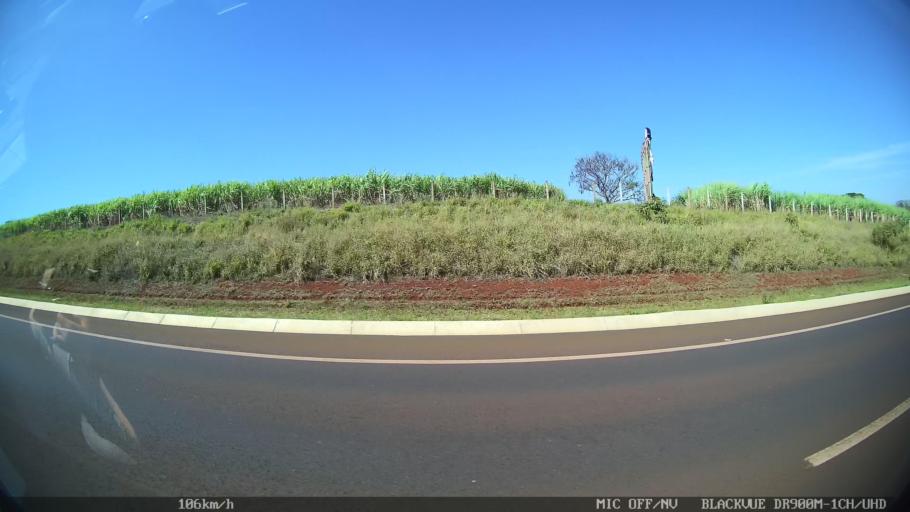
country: BR
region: Sao Paulo
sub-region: Franca
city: Franca
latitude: -20.6543
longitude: -47.4892
